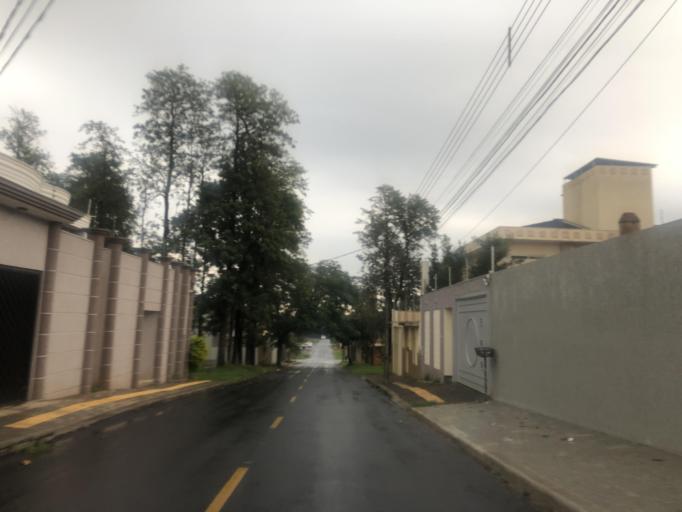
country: BR
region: Parana
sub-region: Foz Do Iguacu
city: Foz do Iguacu
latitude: -25.5188
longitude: -54.5807
